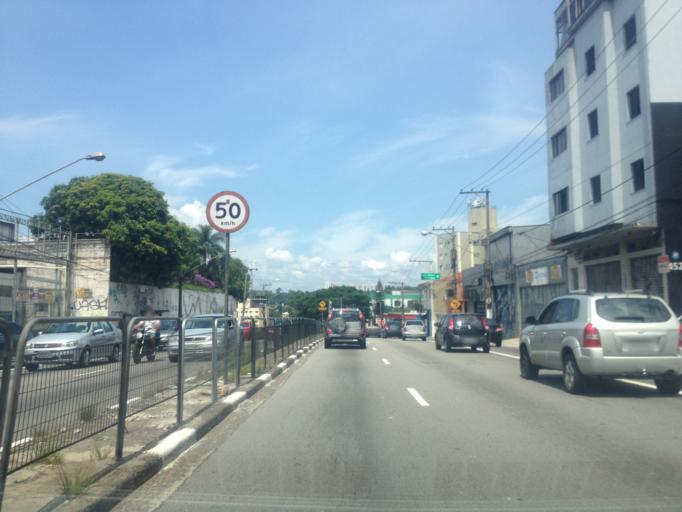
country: BR
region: Sao Paulo
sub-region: Diadema
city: Diadema
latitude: -23.6390
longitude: -46.6728
